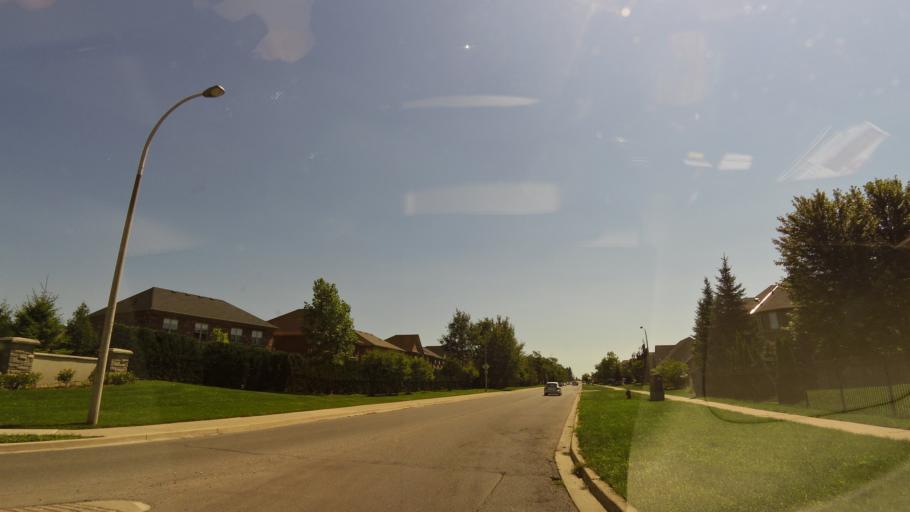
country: CA
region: Ontario
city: Ancaster
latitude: 43.2157
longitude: -79.9555
